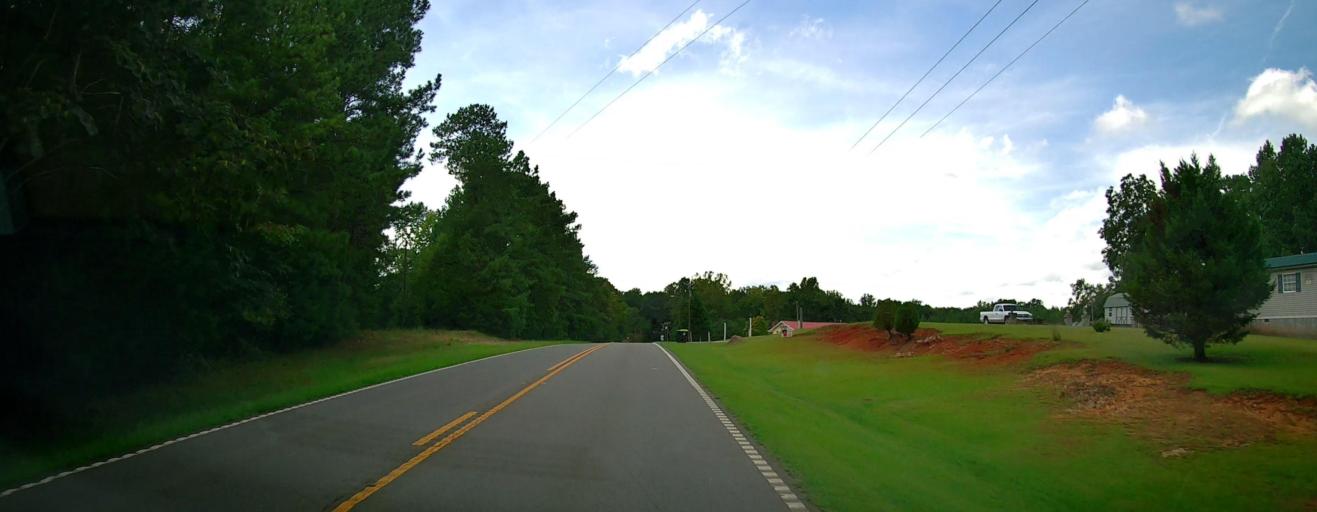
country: US
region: Georgia
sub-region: Talbot County
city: Talbotton
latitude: 32.6710
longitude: -84.5261
